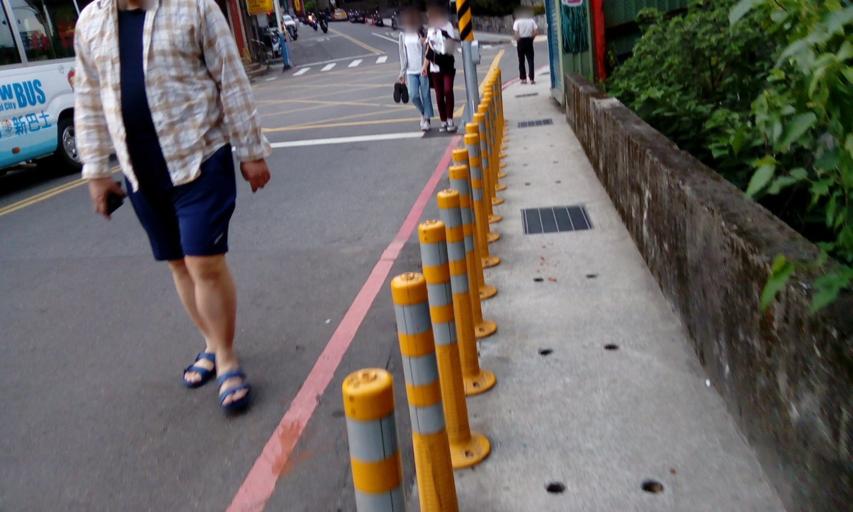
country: TW
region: Taipei
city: Taipei
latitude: 25.1751
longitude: 121.4395
